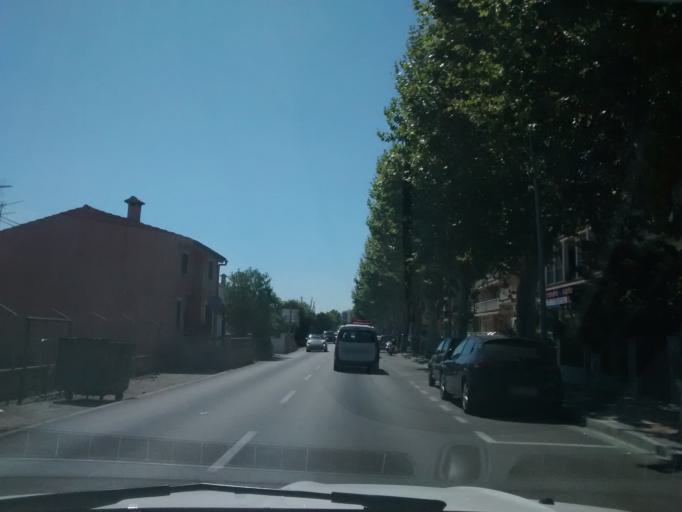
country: ES
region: Balearic Islands
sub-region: Illes Balears
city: Port d'Alcudia
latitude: 39.8456
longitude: 3.1316
